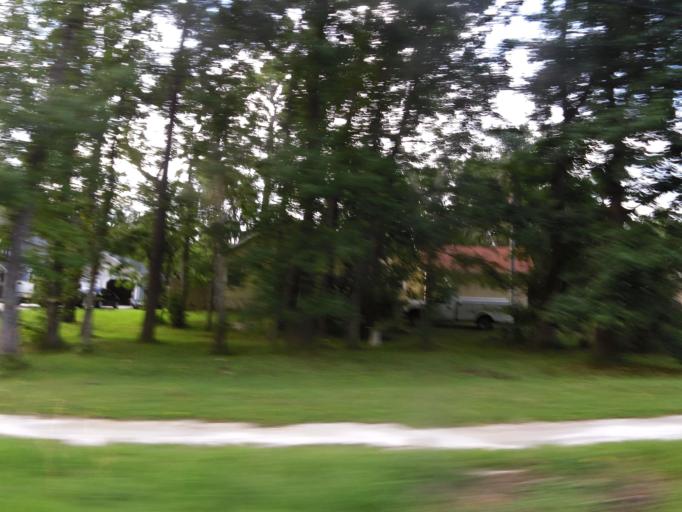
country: US
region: Florida
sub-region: Saint Johns County
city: Fruit Cove
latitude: 30.1390
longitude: -81.6048
